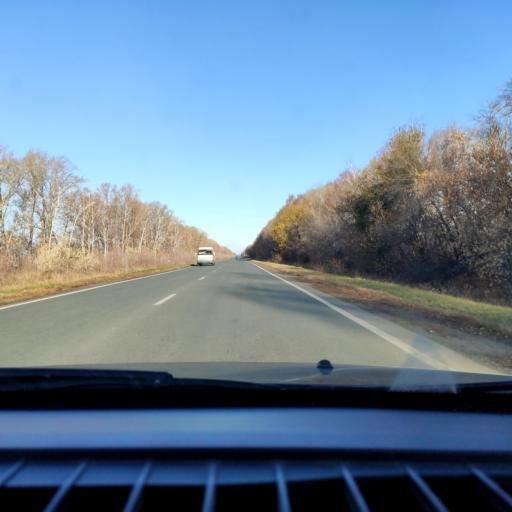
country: RU
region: Samara
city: Tol'yatti
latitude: 53.6007
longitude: 49.3226
